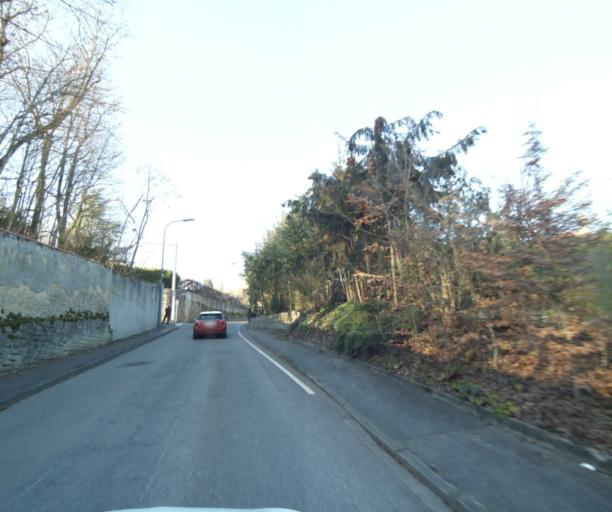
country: FR
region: Lorraine
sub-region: Departement de Meurthe-et-Moselle
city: Saint-Max
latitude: 48.7106
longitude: 6.2146
